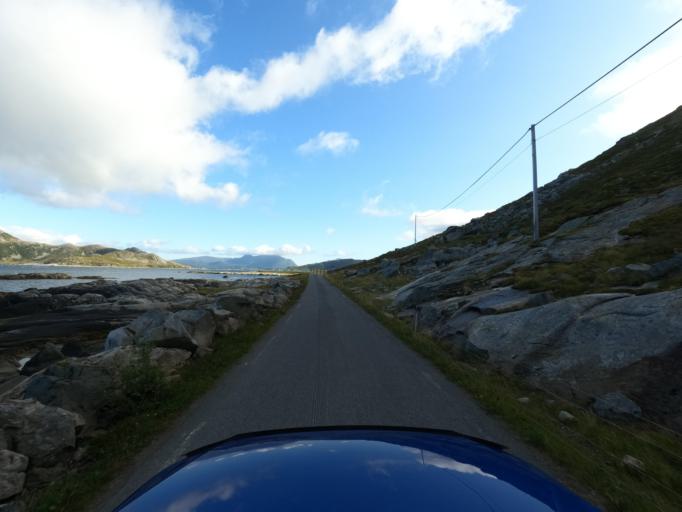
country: NO
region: Nordland
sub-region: Vestvagoy
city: Gravdal
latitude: 68.1489
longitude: 13.4384
